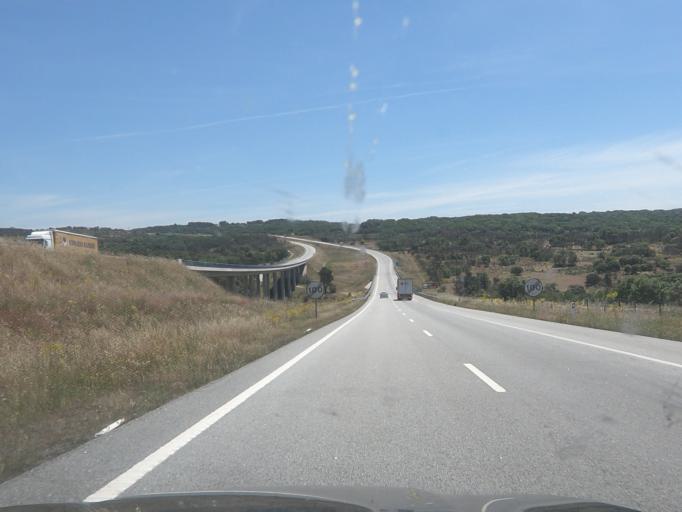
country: PT
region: Guarda
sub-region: Pinhel
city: Pinhel
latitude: 40.6047
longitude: -7.0352
